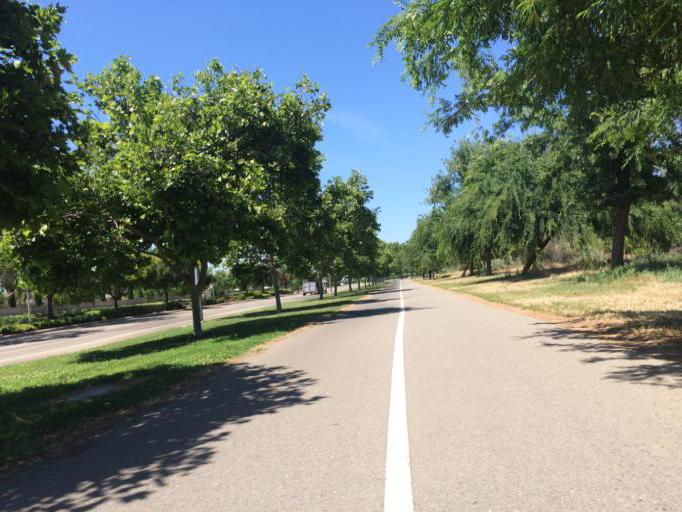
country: US
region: California
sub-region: Fresno County
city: Clovis
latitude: 36.8500
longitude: -119.7027
